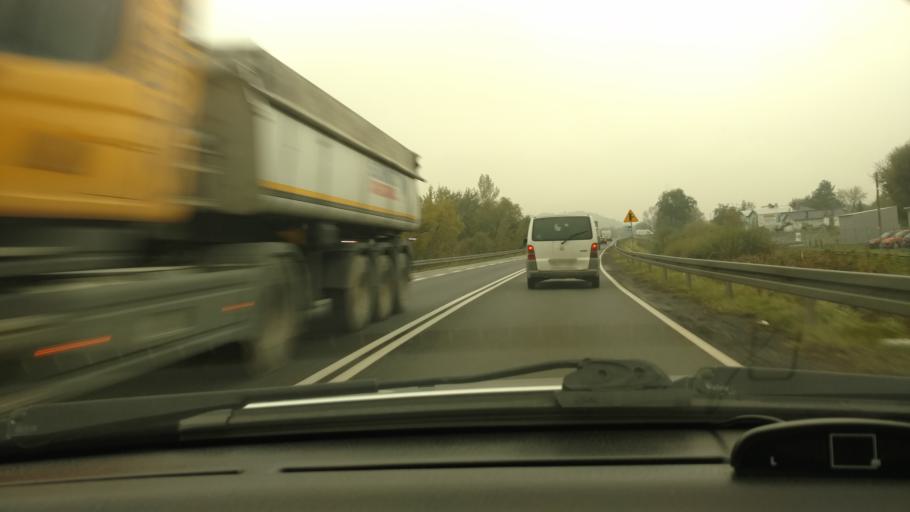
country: PL
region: Lesser Poland Voivodeship
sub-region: Powiat gorlicki
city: Kobylanka
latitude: 49.6745
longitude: 21.1894
